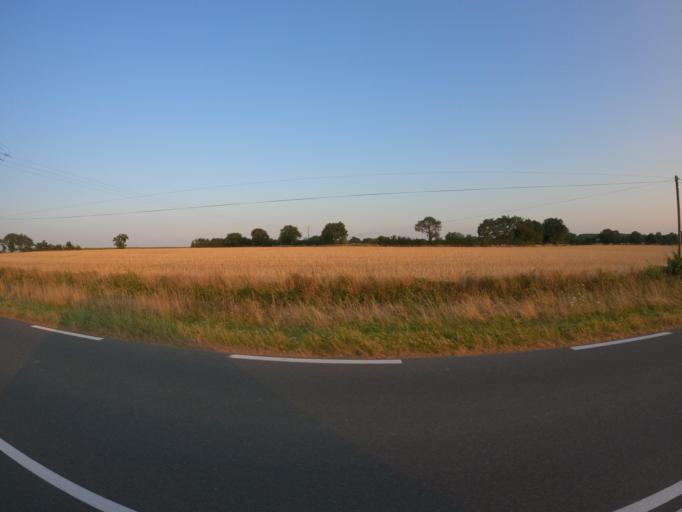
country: FR
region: Pays de la Loire
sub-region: Departement de la Mayenne
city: Meslay-du-Maine
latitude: 47.8680
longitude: -0.5479
